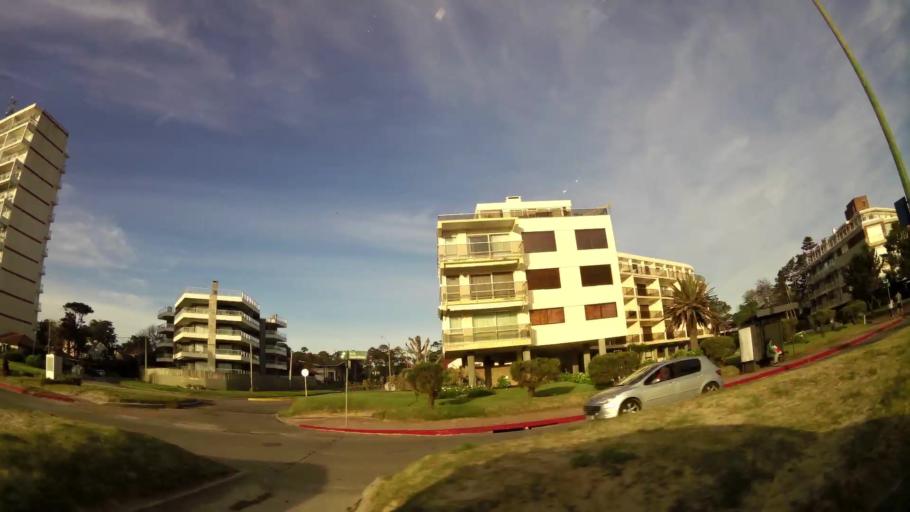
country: UY
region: Maldonado
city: Punta del Este
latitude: -34.9399
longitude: -54.9477
